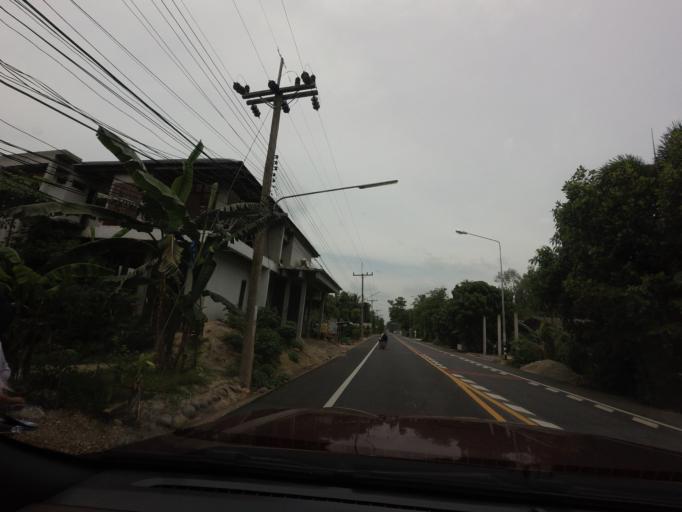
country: TH
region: Pattani
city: Yaring
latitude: 6.8577
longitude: 101.3624
